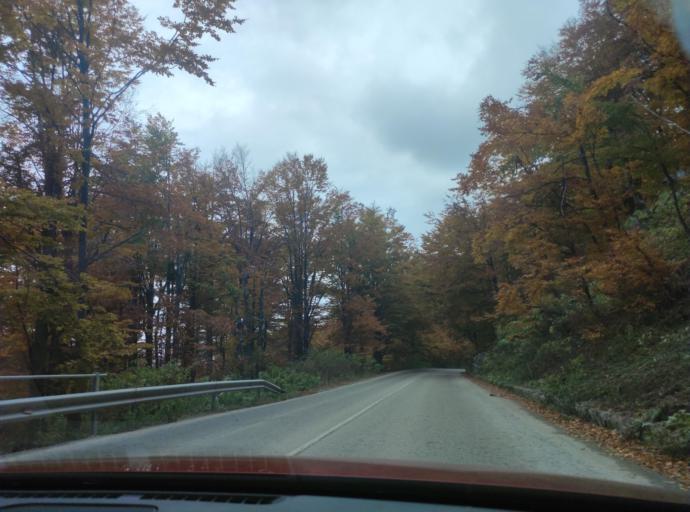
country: BG
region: Montana
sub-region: Obshtina Berkovitsa
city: Berkovitsa
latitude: 43.1278
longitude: 23.1400
